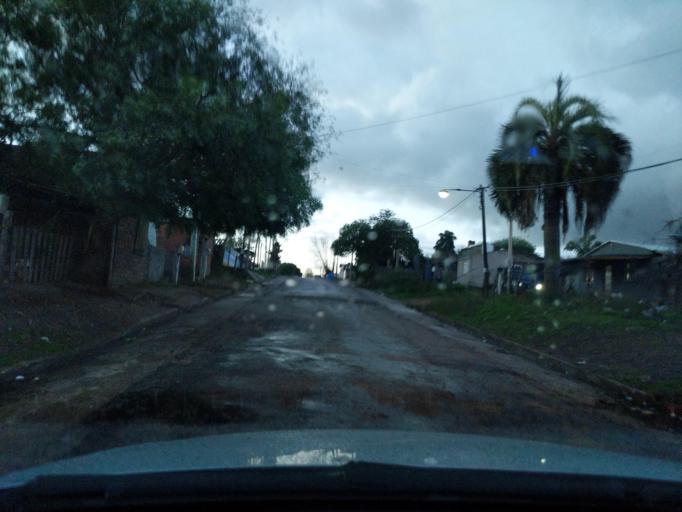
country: UY
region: Florida
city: Florida
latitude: -34.1099
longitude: -56.2110
